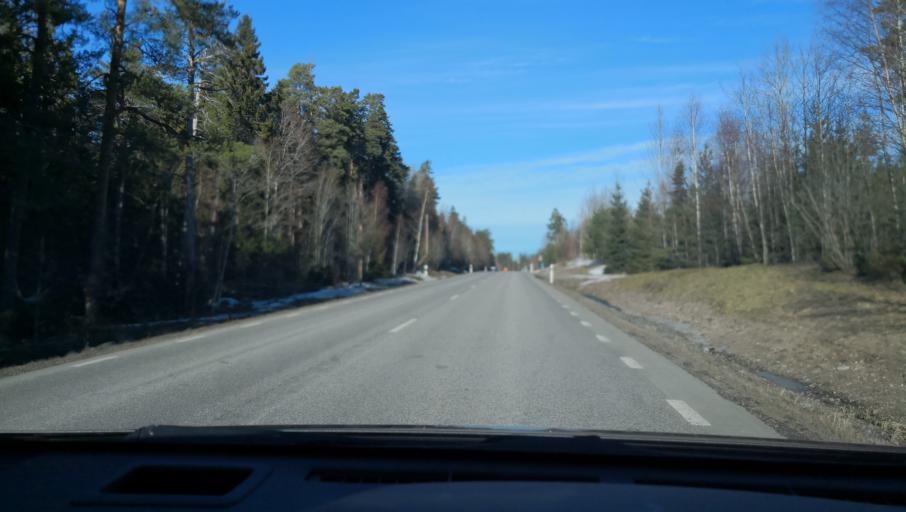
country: SE
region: Uppsala
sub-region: Uppsala Kommun
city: Vattholma
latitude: 60.0679
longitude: 17.7573
